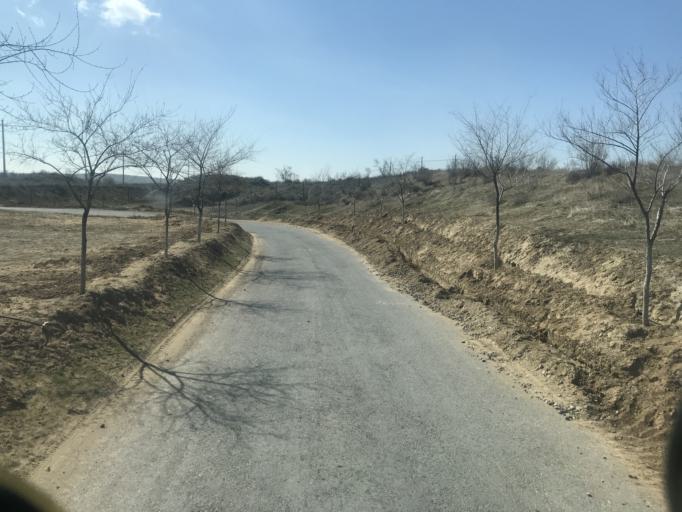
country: KZ
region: Ongtustik Qazaqstan
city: Shardara
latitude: 41.2487
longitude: 67.9019
